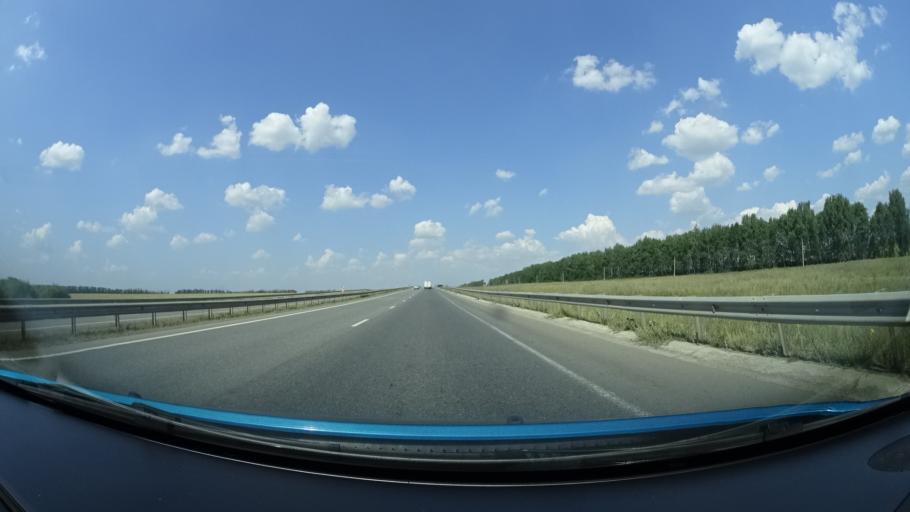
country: RU
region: Bashkortostan
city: Dmitriyevka
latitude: 54.6875
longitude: 55.3078
